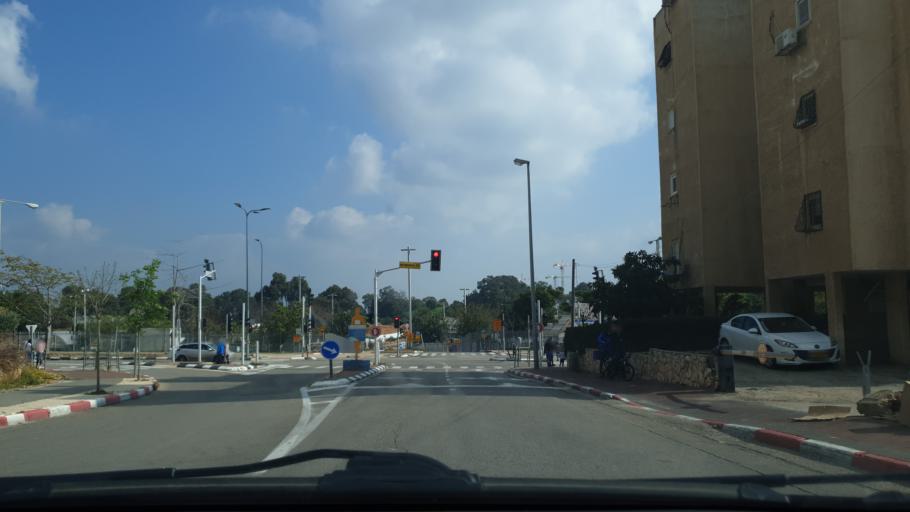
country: IL
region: Central District
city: Bet Dagan
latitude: 31.9668
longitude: 34.8245
